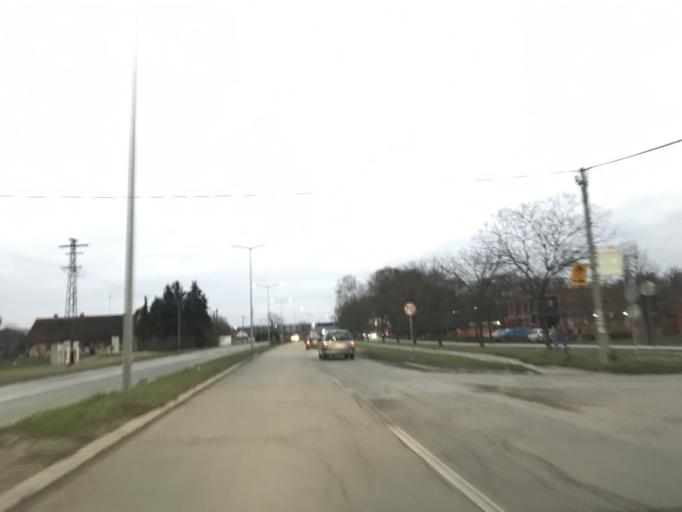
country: RS
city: Veternik
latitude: 45.2793
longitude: 19.7911
